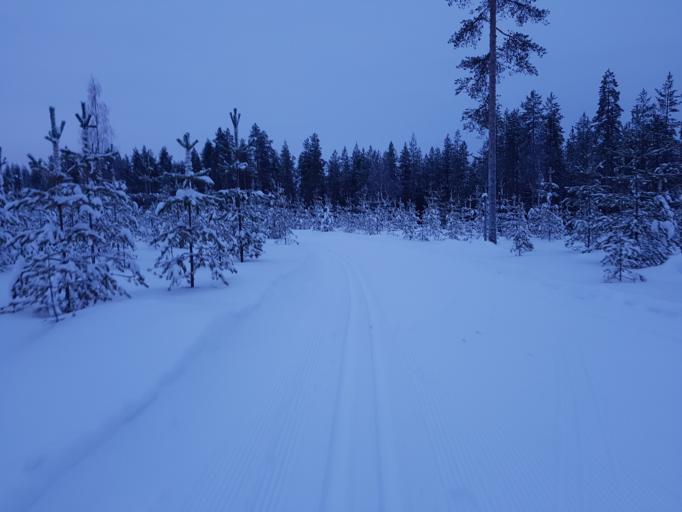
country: FI
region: Kainuu
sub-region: Kehys-Kainuu
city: Kuhmo
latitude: 64.0864
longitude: 29.5170
